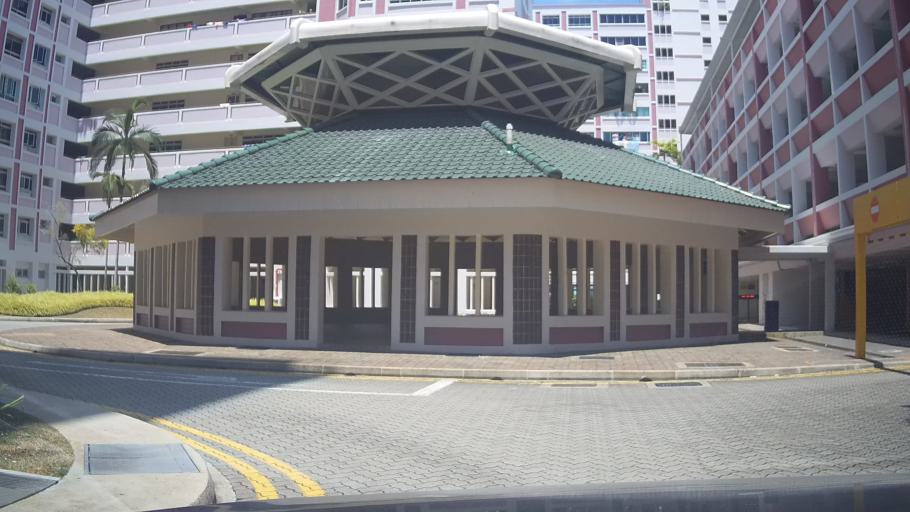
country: MY
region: Johor
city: Kampung Pasir Gudang Baru
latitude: 1.3707
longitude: 103.9632
